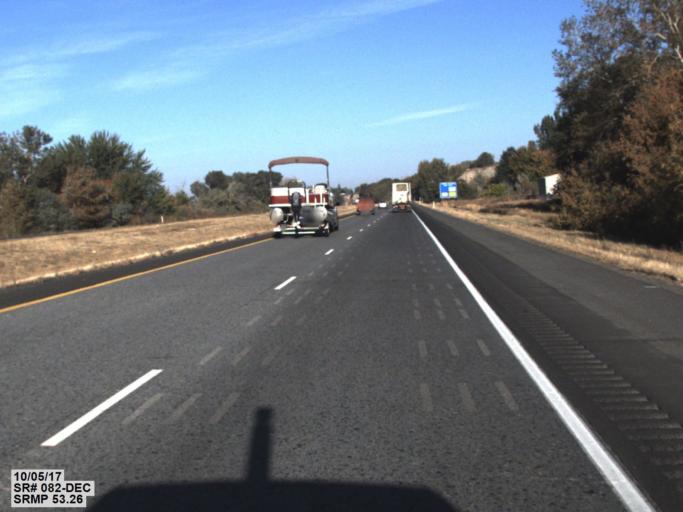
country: US
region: Washington
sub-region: Yakima County
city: Zillah
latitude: 46.3968
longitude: -120.2564
